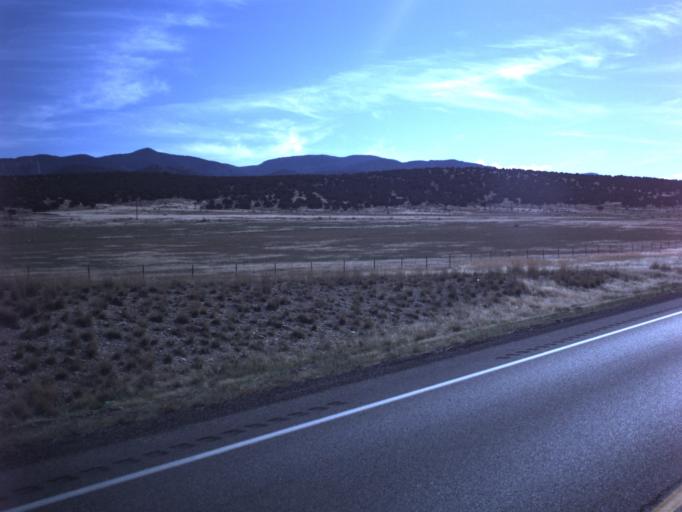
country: US
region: Utah
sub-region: Sanpete County
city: Gunnison
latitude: 39.3353
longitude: -111.9179
